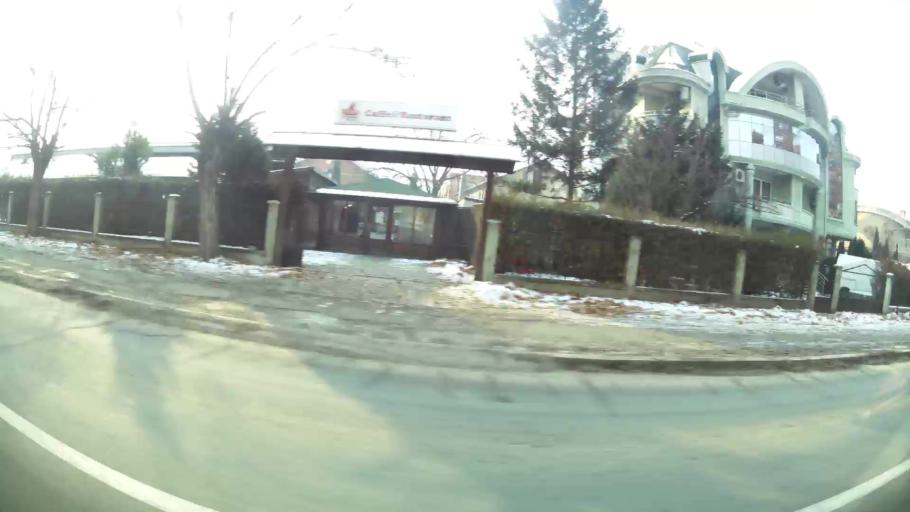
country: MK
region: Butel
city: Butel
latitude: 42.0244
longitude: 21.4493
